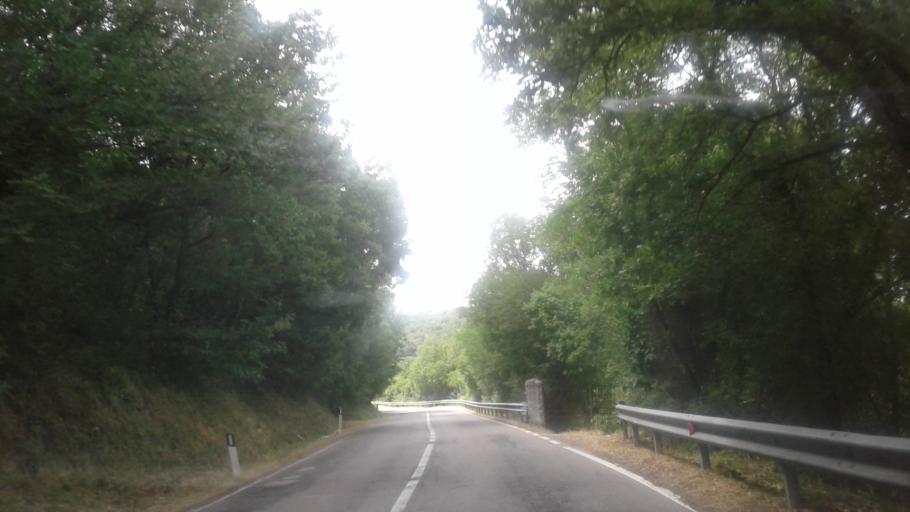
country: IT
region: Sardinia
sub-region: Provincia di Olbia-Tempio
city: Tempio Pausania
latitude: 40.9109
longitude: 9.0830
